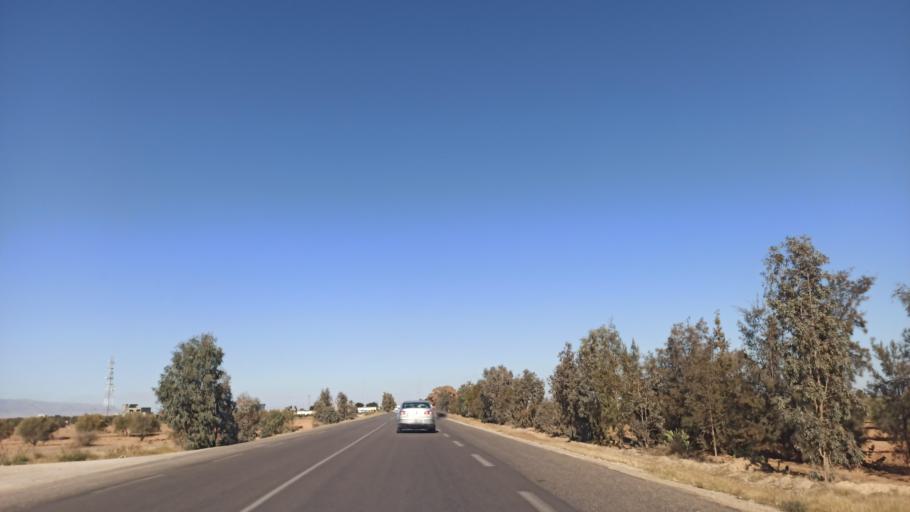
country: TN
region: Sidi Bu Zayd
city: Jilma
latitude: 35.1424
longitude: 9.3620
